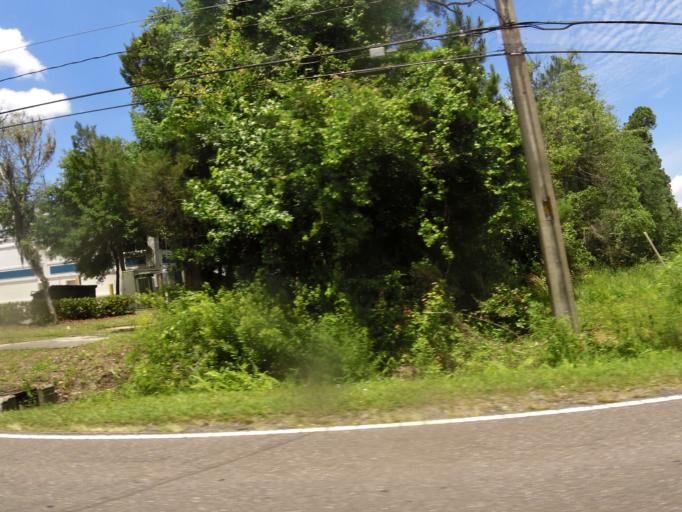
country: US
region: Florida
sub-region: Duval County
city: Jacksonville
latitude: 30.4696
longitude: -81.6134
